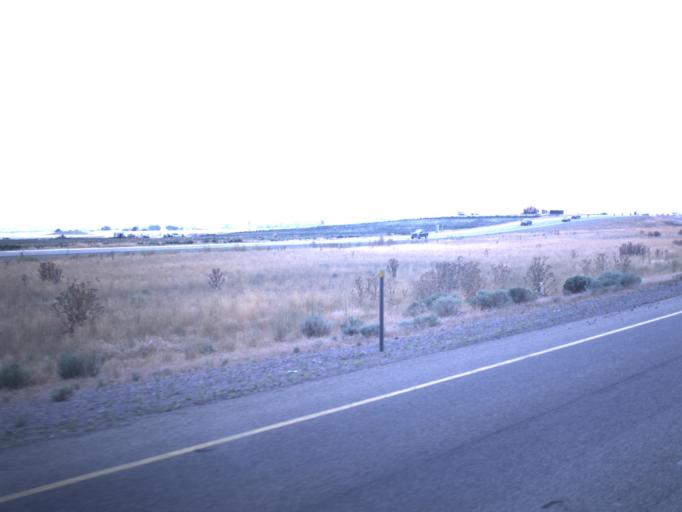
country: US
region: Utah
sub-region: Salt Lake County
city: Herriman
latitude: 40.5150
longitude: -112.0058
